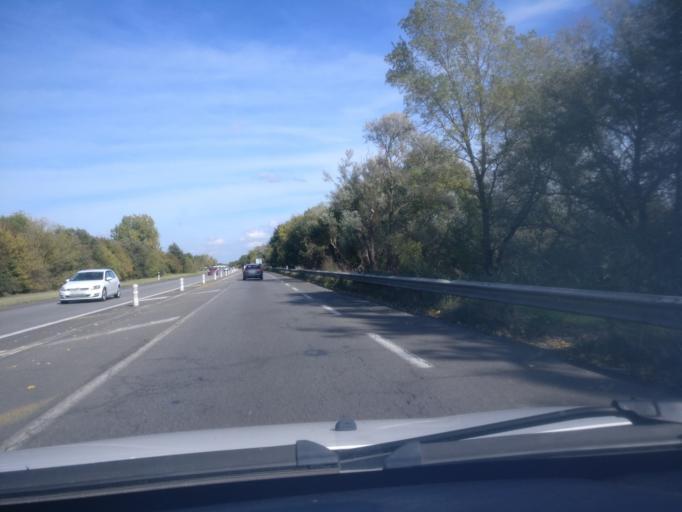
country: FR
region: Pays de la Loire
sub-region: Departement de la Loire-Atlantique
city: Sainte-Luce-sur-Loire
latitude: 47.2295
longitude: -1.4892
